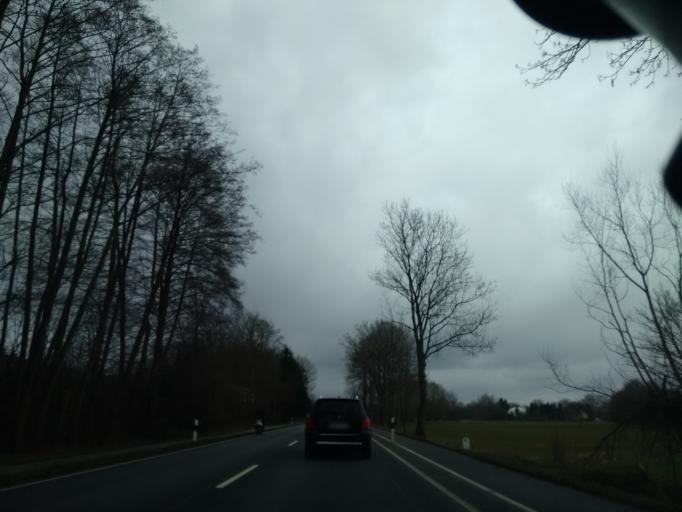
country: DE
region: North Rhine-Westphalia
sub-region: Regierungsbezirk Detmold
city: Paderborn
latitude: 51.7554
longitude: 8.7804
